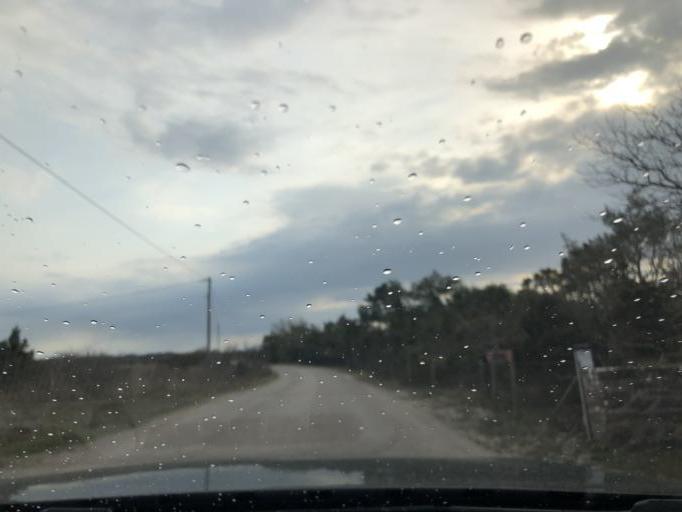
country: SE
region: Kalmar
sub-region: Borgholms Kommun
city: Borgholm
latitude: 57.2240
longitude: 16.9549
